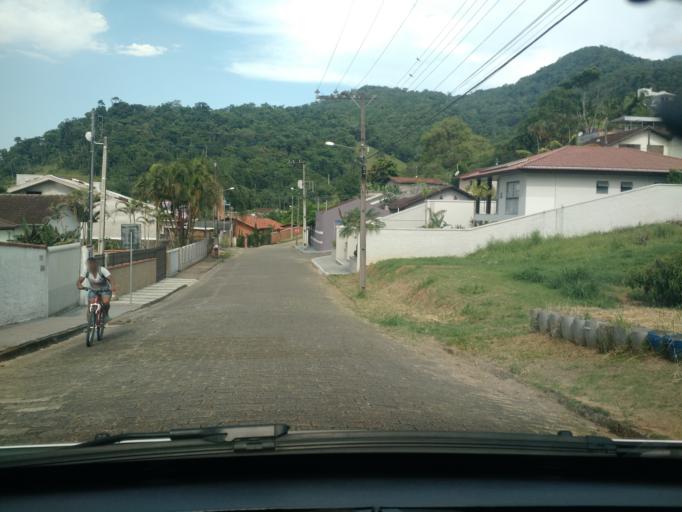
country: BR
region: Santa Catarina
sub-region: Jaragua Do Sul
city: Jaragua do Sul
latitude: -26.5079
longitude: -49.0894
